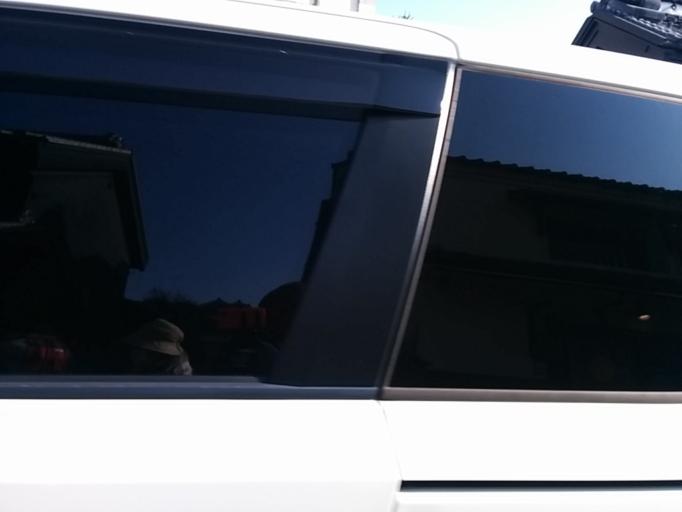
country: JP
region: Saitama
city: Kawagoe
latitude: 35.9226
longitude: 139.4828
